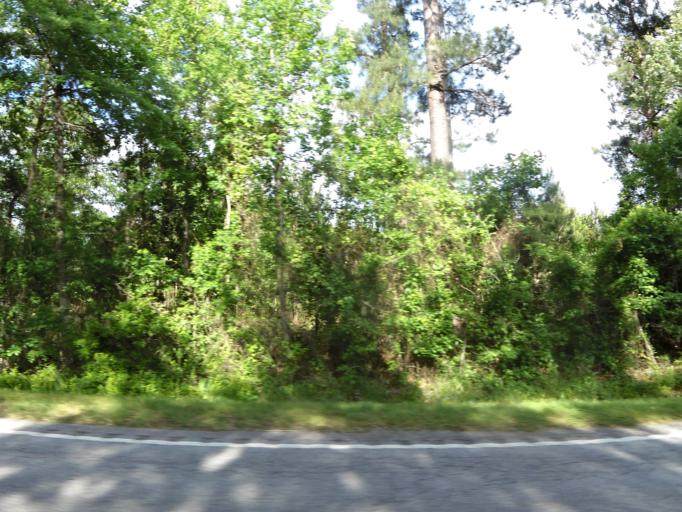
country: US
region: South Carolina
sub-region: Allendale County
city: Fairfax
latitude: 32.8734
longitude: -81.2384
